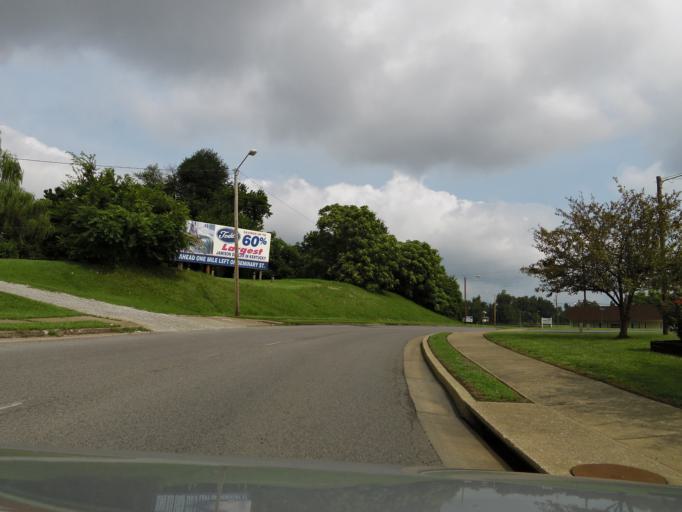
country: US
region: Kentucky
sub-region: Hopkins County
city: Madisonville
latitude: 37.3279
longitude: -87.4868
